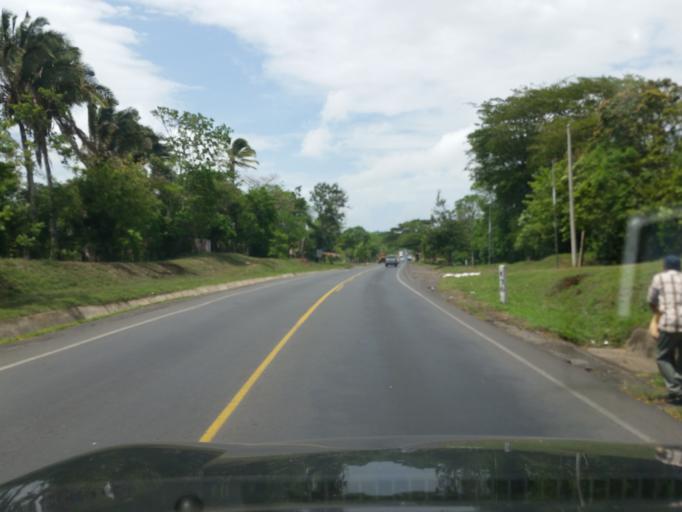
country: NI
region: Masaya
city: Masaya
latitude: 11.9448
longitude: -86.0912
